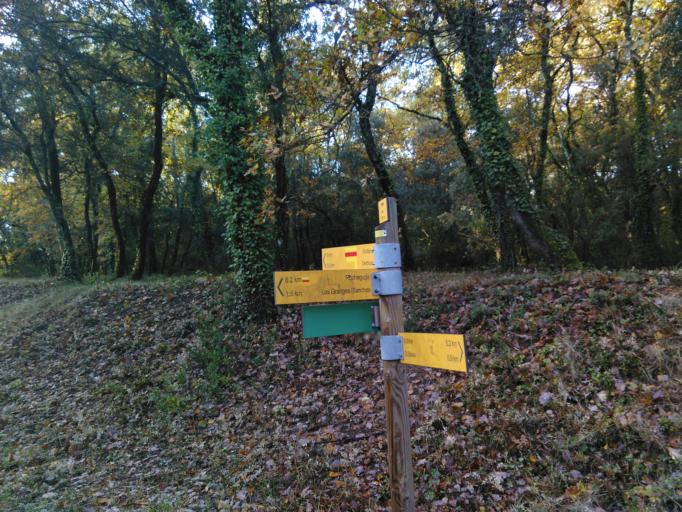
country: FR
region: Rhone-Alpes
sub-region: Departement de la Drome
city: Rochegude
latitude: 44.2666
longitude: 4.7940
